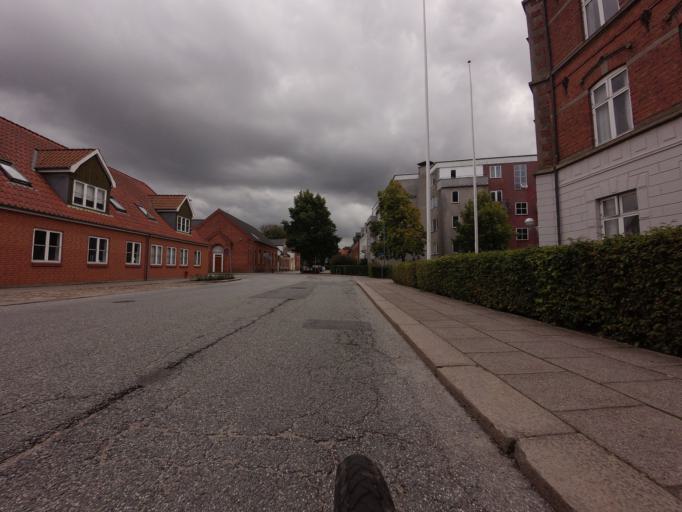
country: DK
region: North Denmark
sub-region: Hjorring Kommune
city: Hjorring
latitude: 57.4579
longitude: 9.9839
